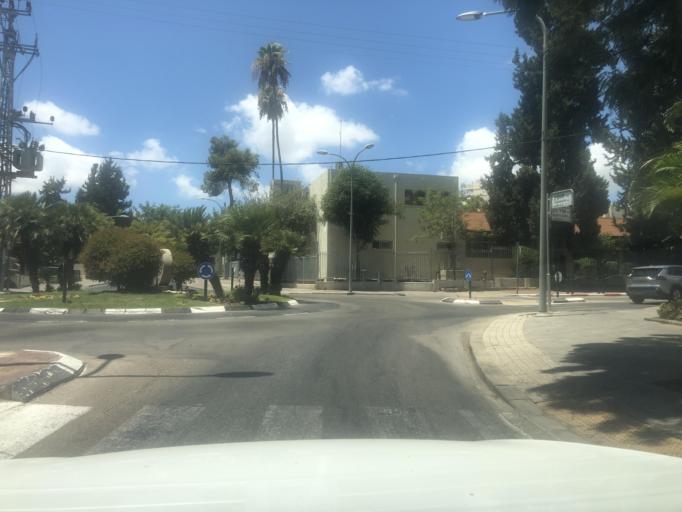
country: IL
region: Central District
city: Hod HaSharon
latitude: 32.1600
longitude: 34.9046
